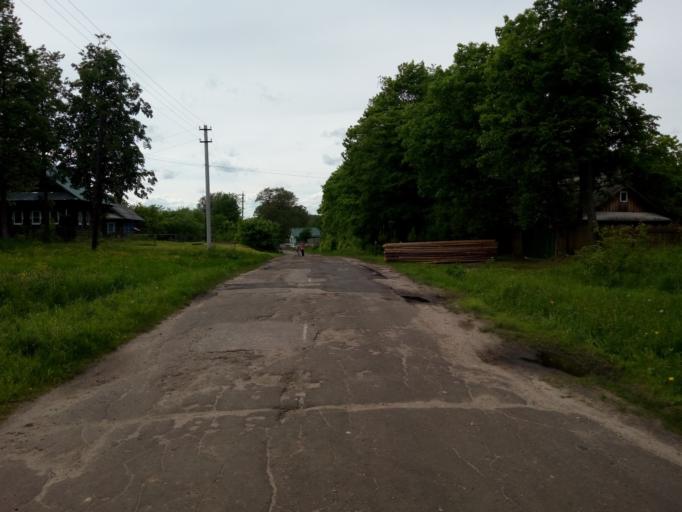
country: RU
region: Nizjnij Novgorod
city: Voskresenskoye
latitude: 56.7787
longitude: 45.5379
